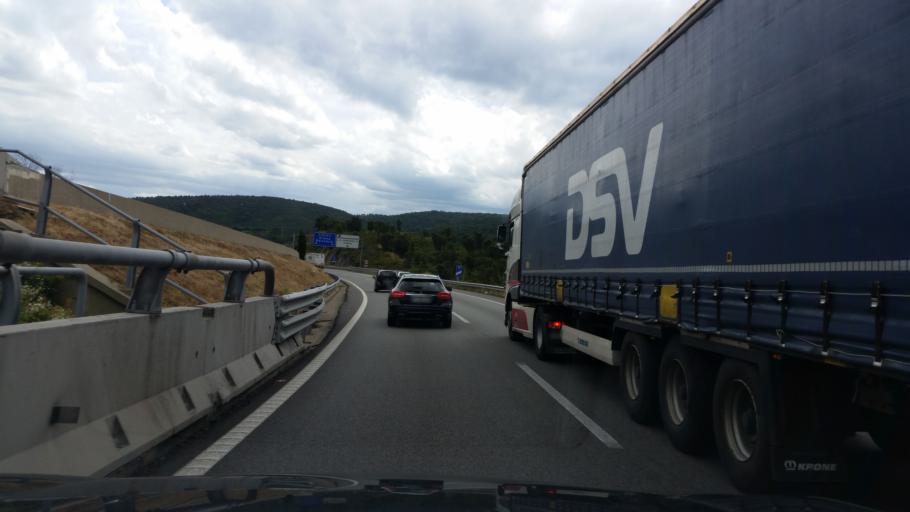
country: ES
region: Catalonia
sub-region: Provincia de Girona
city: la Jonquera
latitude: 42.4371
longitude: 2.8649
